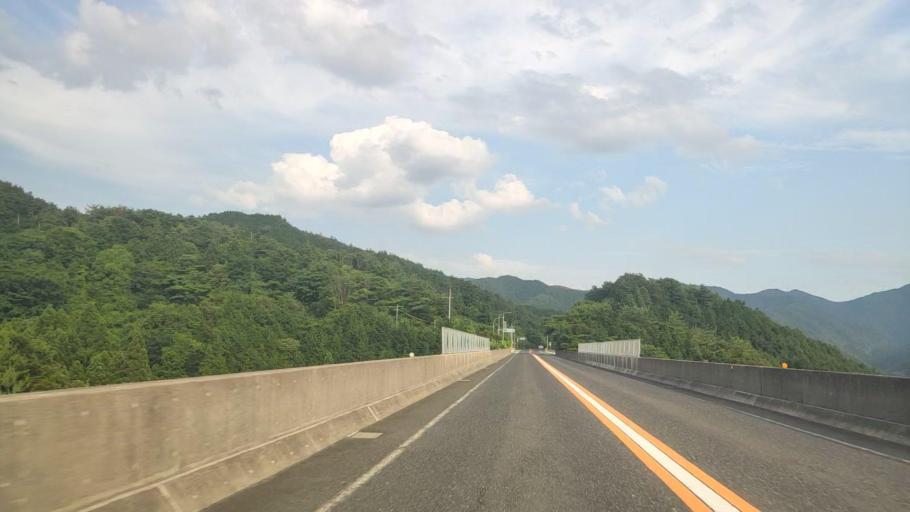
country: JP
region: Tottori
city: Kurayoshi
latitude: 35.3405
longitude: 133.7505
